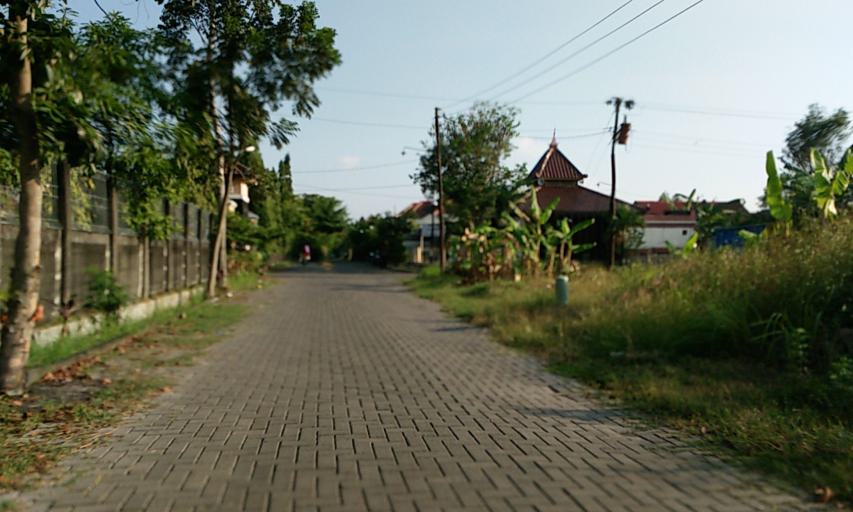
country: ID
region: Central Java
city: Mranggen
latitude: -7.0118
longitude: 110.4857
